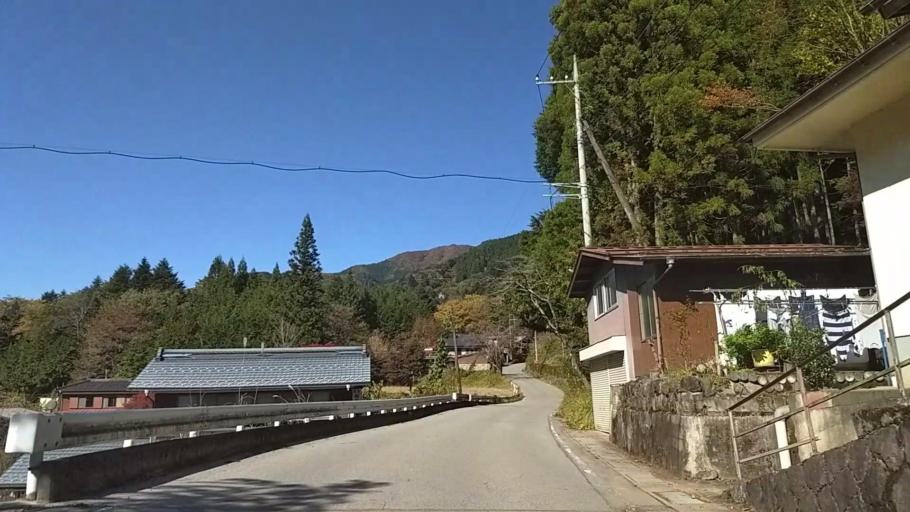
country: JP
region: Yamanashi
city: Uenohara
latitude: 35.7002
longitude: 139.0235
